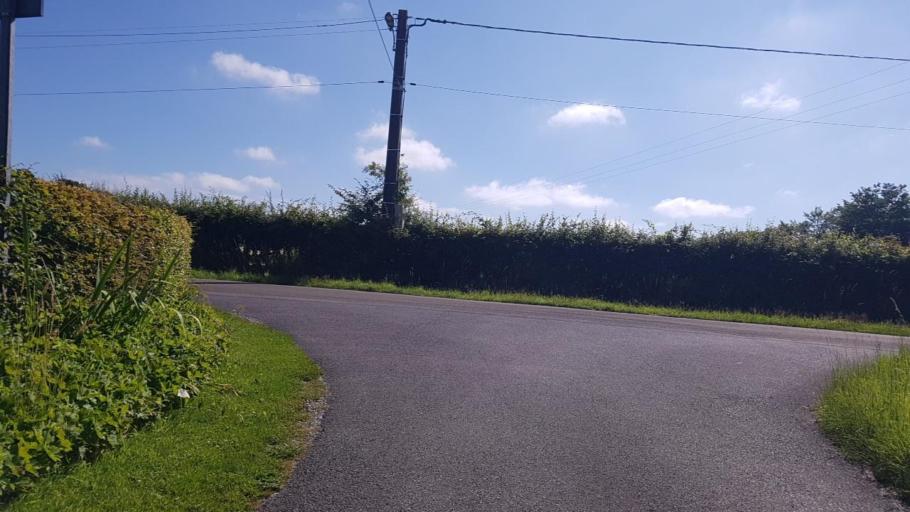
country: FR
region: Nord-Pas-de-Calais
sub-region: Departement du Nord
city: Anor
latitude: 49.9888
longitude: 4.1323
